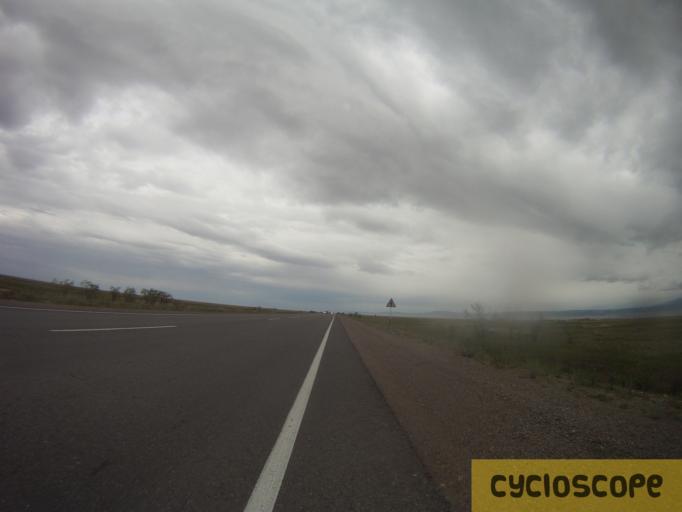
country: KG
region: Chuy
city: Ivanovka
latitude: 43.4074
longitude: 75.0835
